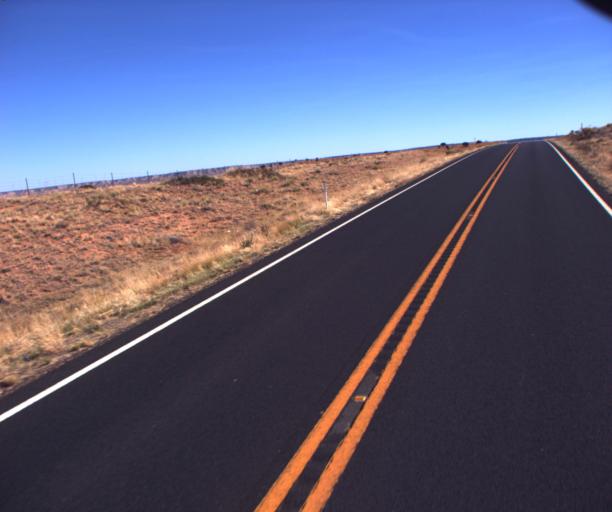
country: US
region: Arizona
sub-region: Apache County
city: Ganado
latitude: 35.7858
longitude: -109.6699
